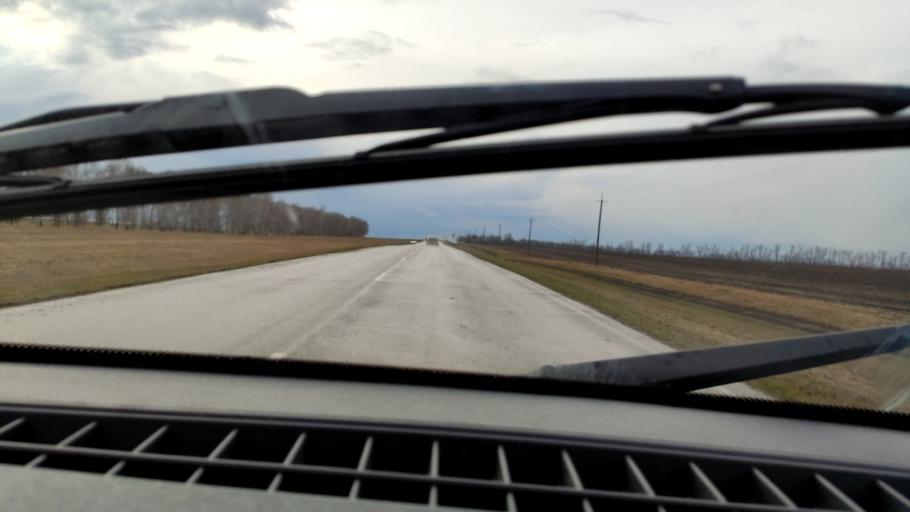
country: RU
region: Bashkortostan
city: Kushnarenkovo
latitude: 55.1009
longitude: 55.0401
